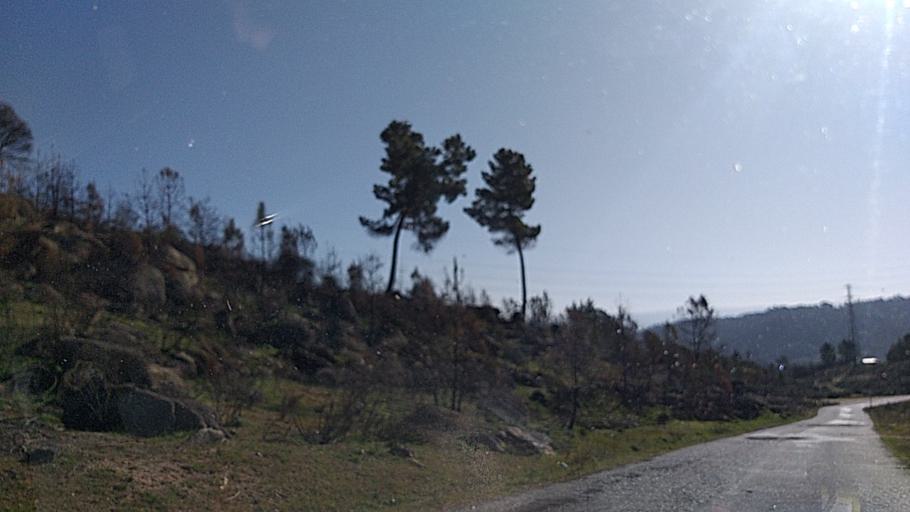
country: PT
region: Guarda
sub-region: Celorico da Beira
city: Celorico da Beira
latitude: 40.6881
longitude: -7.4176
